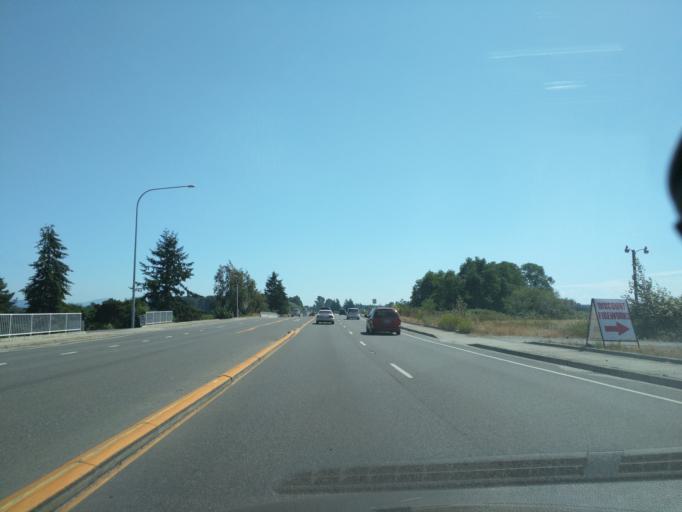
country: US
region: Washington
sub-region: Whatcom County
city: Lynden
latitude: 48.9327
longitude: -122.4855
